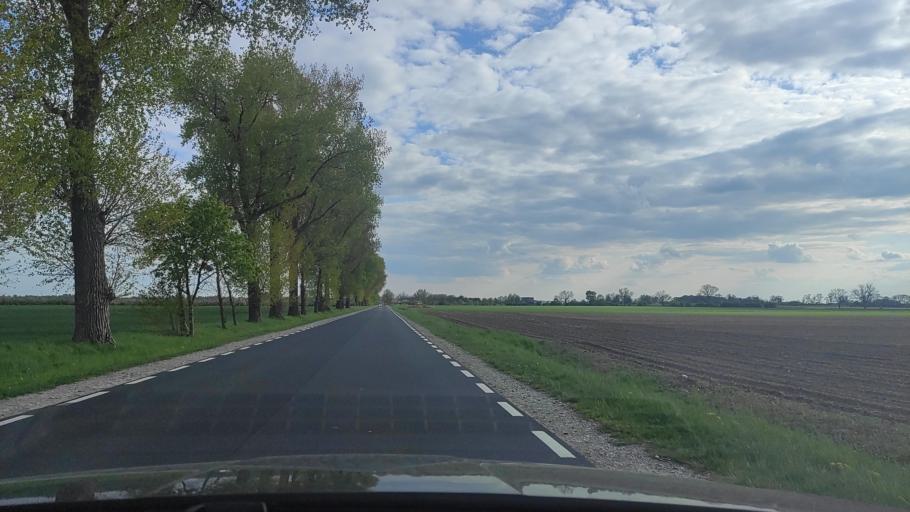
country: PL
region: Greater Poland Voivodeship
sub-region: Powiat poznanski
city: Kostrzyn
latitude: 52.4277
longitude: 17.2300
